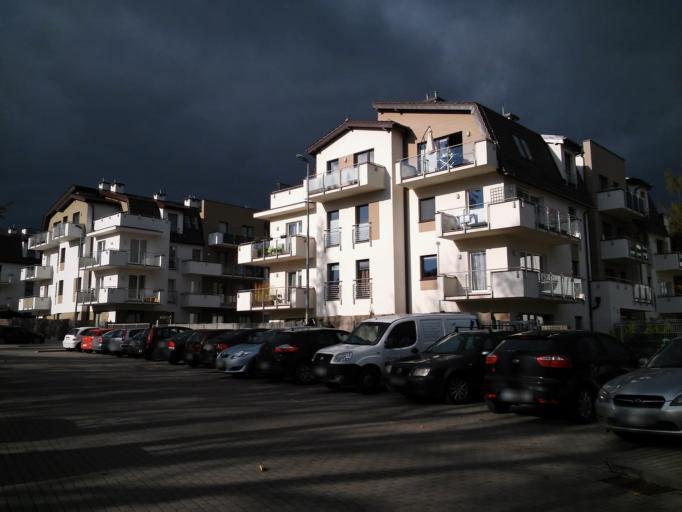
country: PL
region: Pomeranian Voivodeship
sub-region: Powiat gdanski
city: Kowale
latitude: 54.3759
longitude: 18.5793
